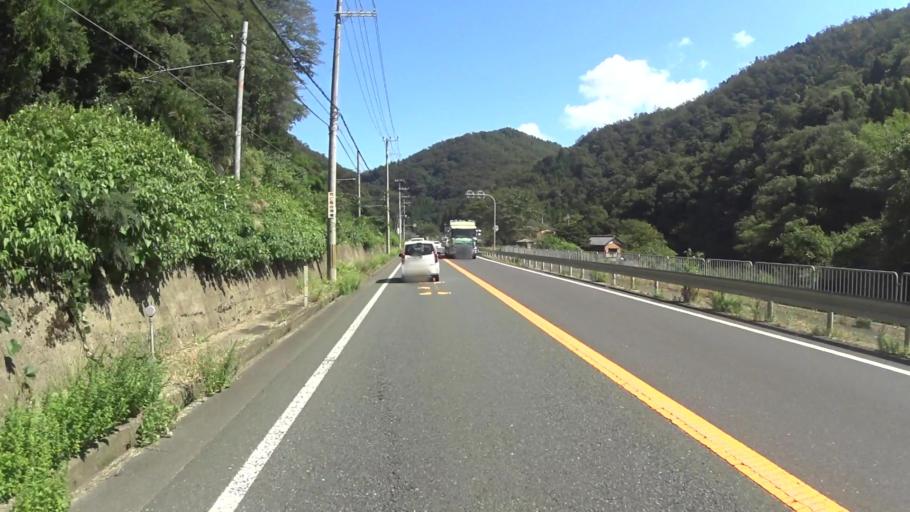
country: JP
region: Kyoto
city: Maizuru
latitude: 35.3887
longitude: 135.3156
